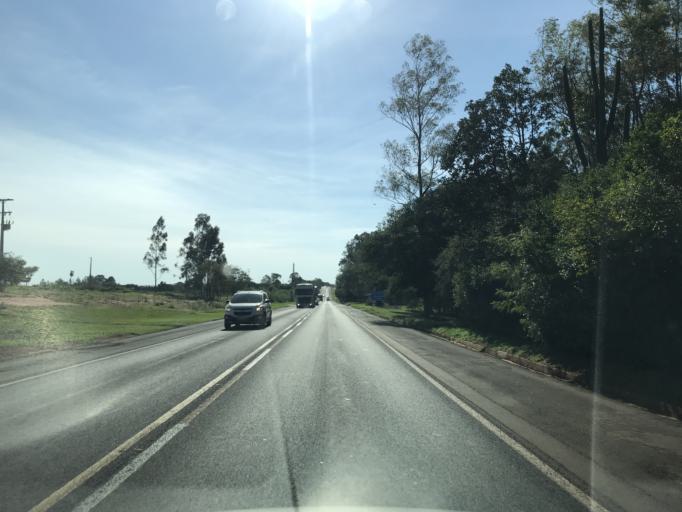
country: BR
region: Parana
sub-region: Umuarama
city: Umuarama
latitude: -23.8394
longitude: -53.3608
